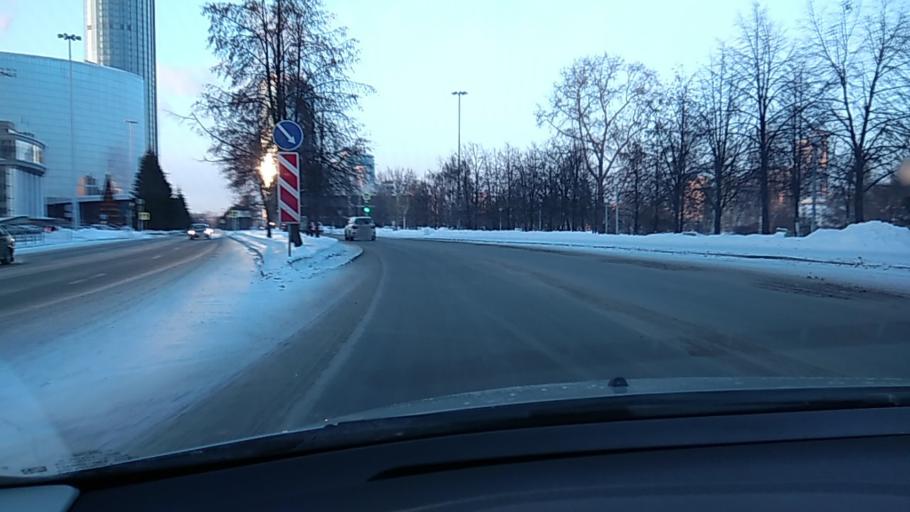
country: RU
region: Sverdlovsk
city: Yekaterinburg
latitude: 56.8413
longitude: 60.5974
